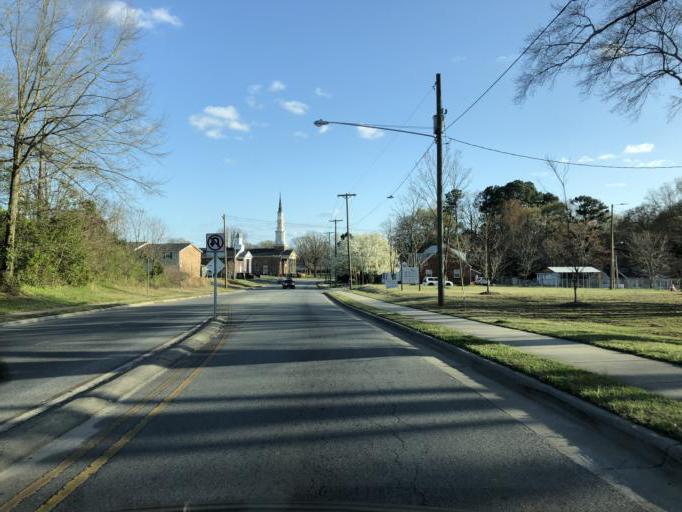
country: US
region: North Carolina
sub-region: Gaston County
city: Gastonia
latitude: 35.2673
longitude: -81.2228
